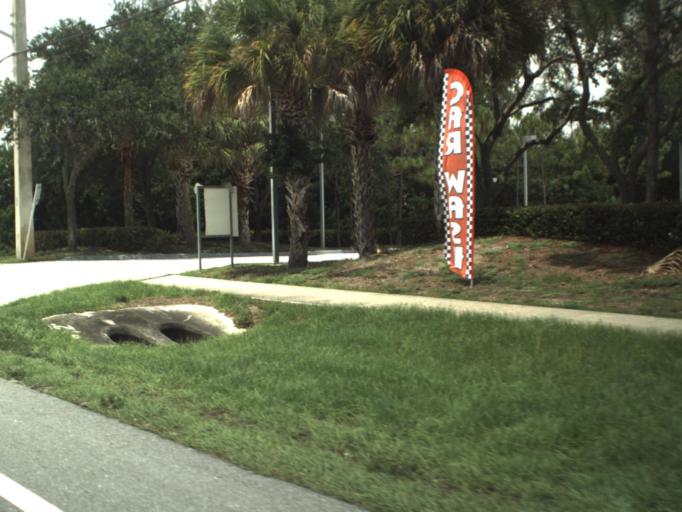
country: US
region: Florida
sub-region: Palm Beach County
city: Villages of Oriole
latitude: 26.4538
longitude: -80.1639
